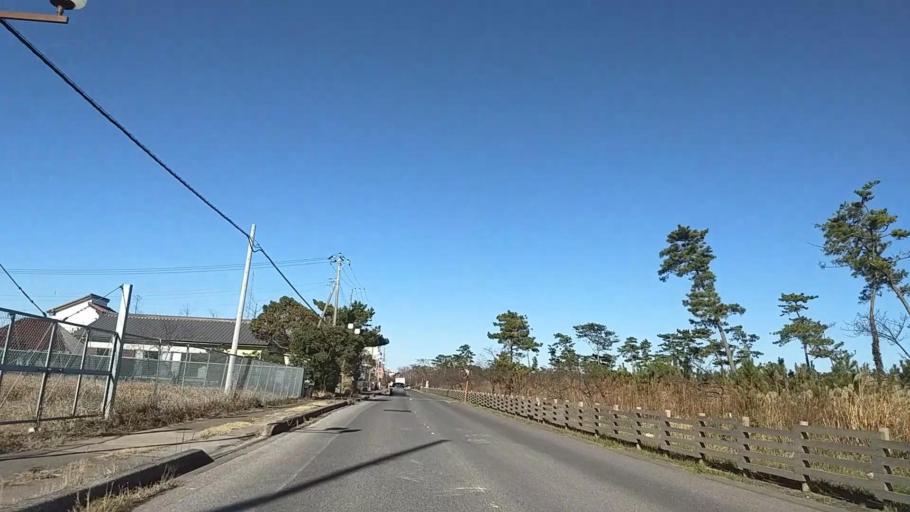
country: JP
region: Chiba
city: Mobara
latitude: 35.4251
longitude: 140.3944
